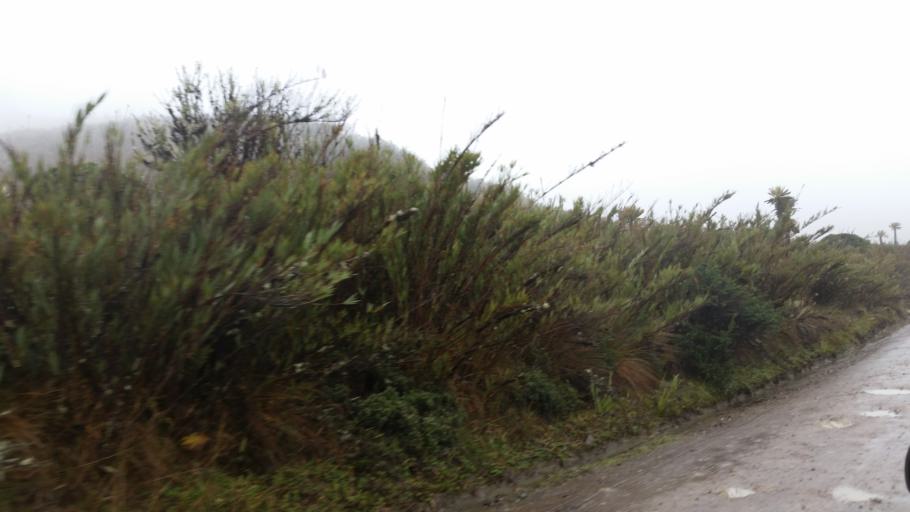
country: CO
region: Cundinamarca
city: La Calera
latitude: 4.6978
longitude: -73.8024
